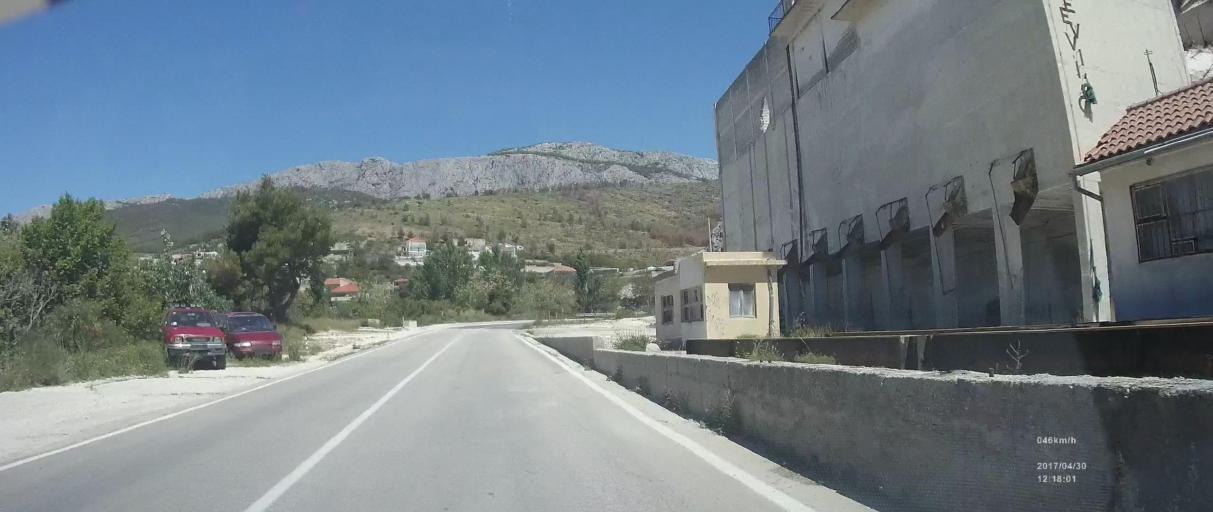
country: HR
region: Splitsko-Dalmatinska
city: Zrnovnica
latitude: 43.5177
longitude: 16.5435
